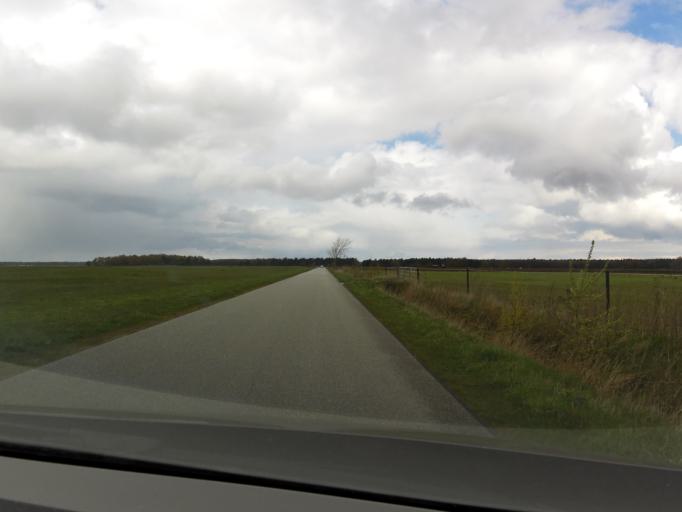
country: DE
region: Mecklenburg-Vorpommern
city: Born
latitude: 54.3853
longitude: 12.5034
